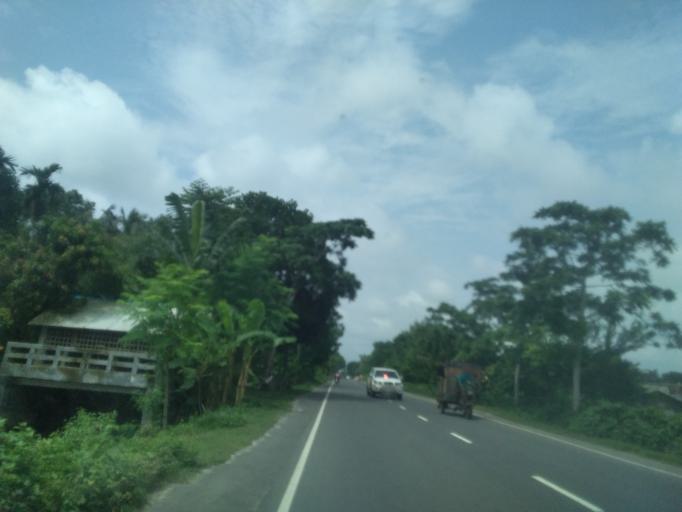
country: BD
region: Khulna
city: Kesabpur
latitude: 22.8067
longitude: 89.2391
